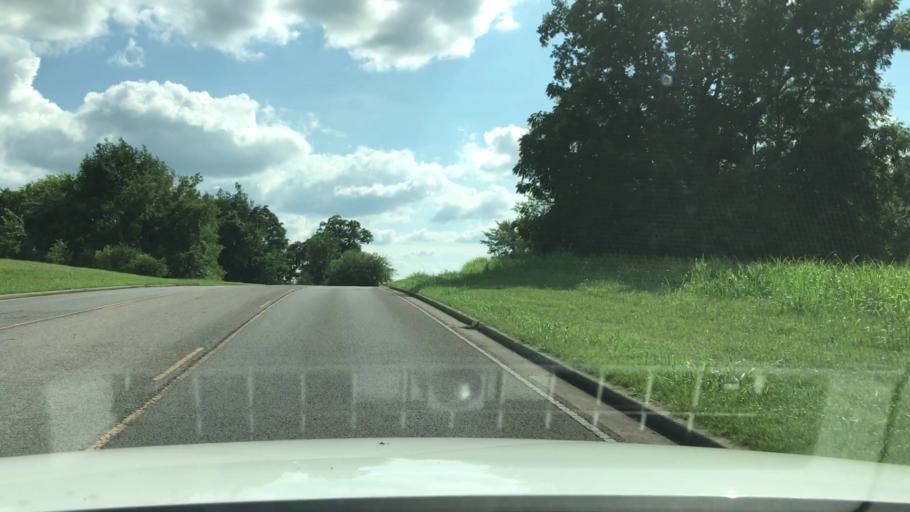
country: US
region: Tennessee
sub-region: Sumner County
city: Gallatin
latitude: 36.3799
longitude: -86.4744
